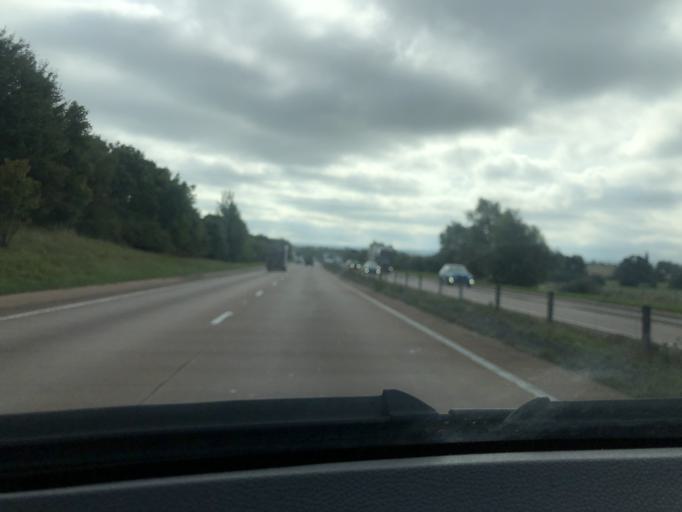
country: GB
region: England
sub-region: Devon
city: Topsham
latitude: 50.7303
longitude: -3.4424
